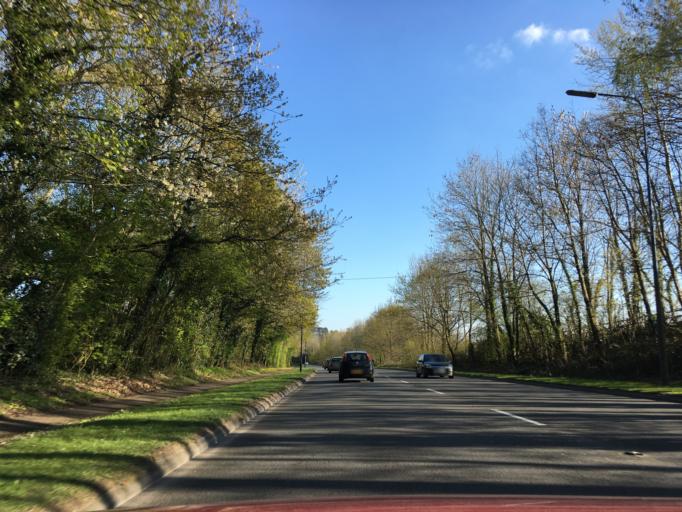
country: GB
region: Wales
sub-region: Torfaen County Borough
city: Cwmbran
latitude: 51.6279
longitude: -3.0173
